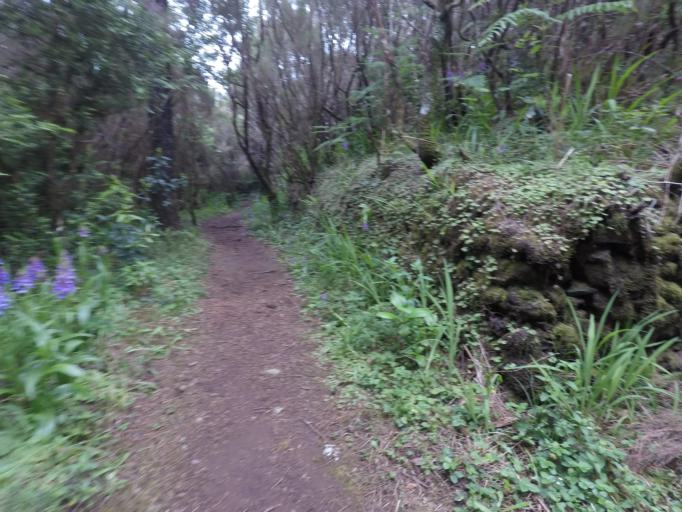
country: PT
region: Madeira
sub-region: Sao Vicente
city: Sao Vicente
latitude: 32.7723
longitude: -17.0627
